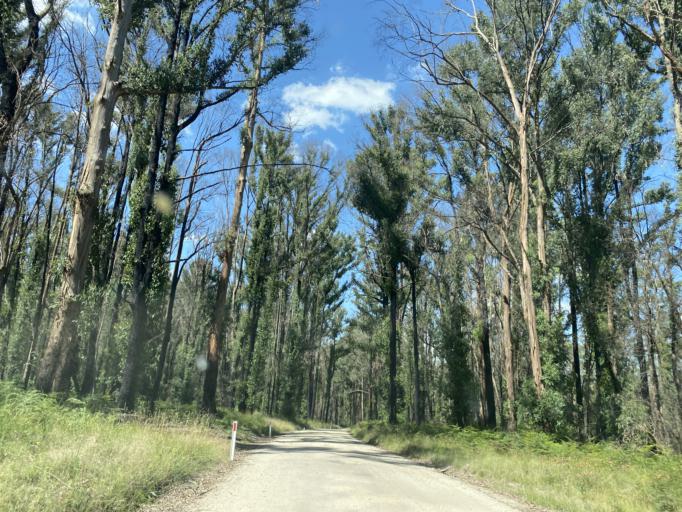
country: AU
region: Victoria
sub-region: Cardinia
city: Gembrook
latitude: -37.9837
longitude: 145.6397
